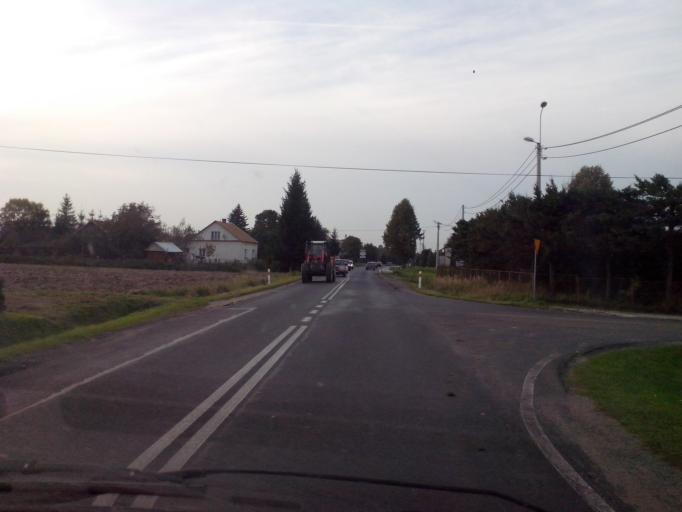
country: PL
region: Subcarpathian Voivodeship
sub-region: Powiat strzyzowski
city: Strzyzow
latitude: 49.8402
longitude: 21.8201
